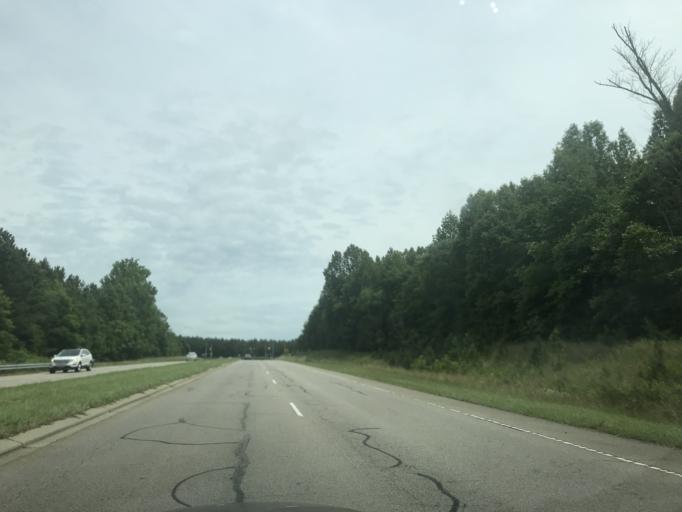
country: US
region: North Carolina
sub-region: Vance County
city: South Henderson
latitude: 36.2975
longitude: -78.4310
